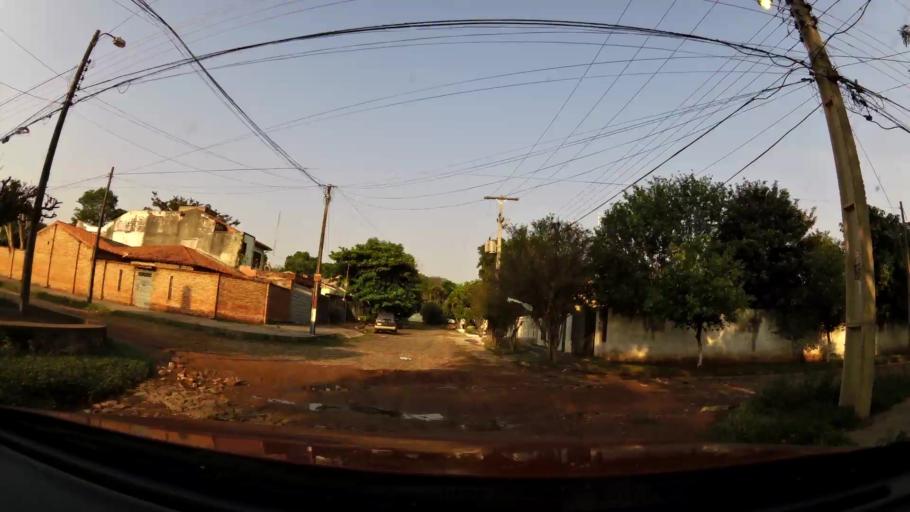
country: PY
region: Central
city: Lambare
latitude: -25.3479
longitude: -57.6036
